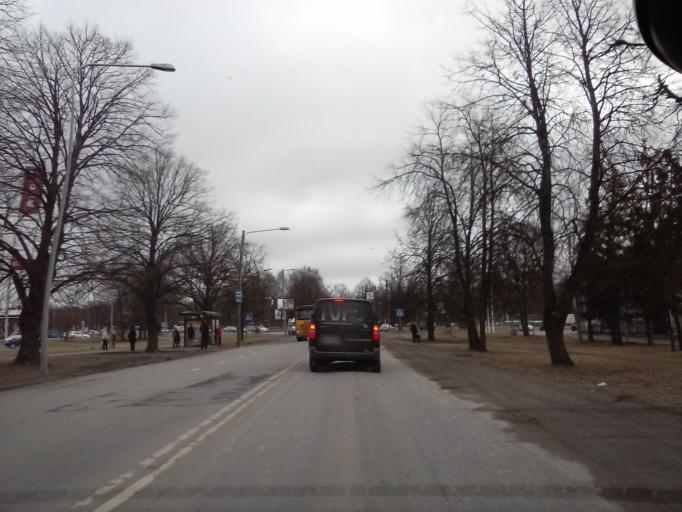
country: EE
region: Harju
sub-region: Saue vald
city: Laagri
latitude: 59.4238
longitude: 24.6435
